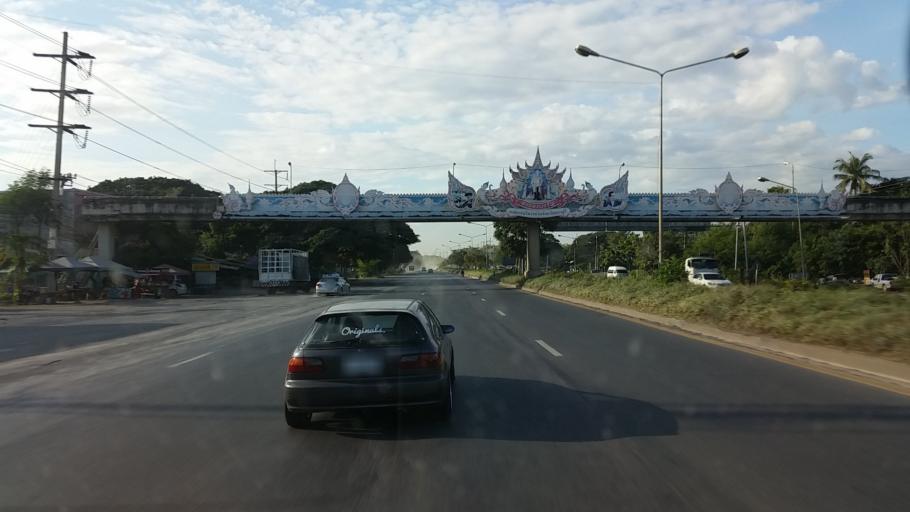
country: TH
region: Sara Buri
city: Chaloem Phra Kiat
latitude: 14.6621
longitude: 100.8870
